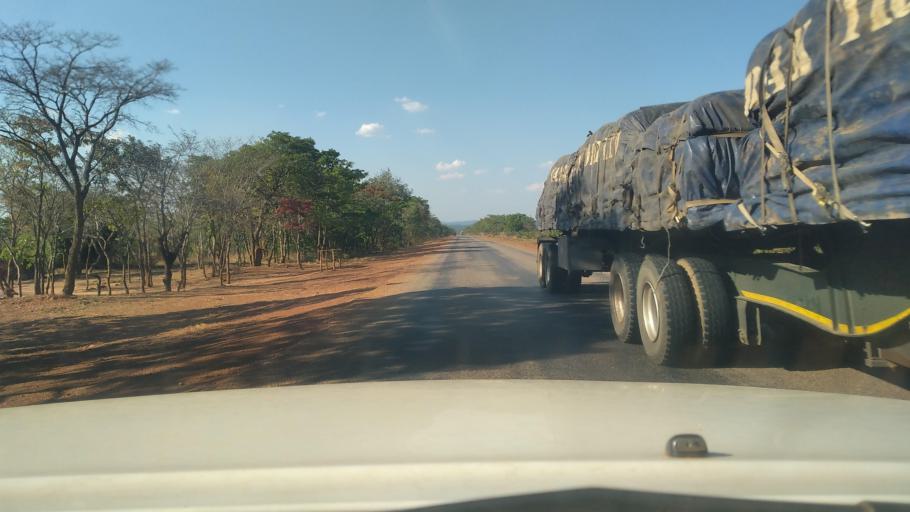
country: ZM
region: Northern
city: Mpika
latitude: -11.7719
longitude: 31.4619
